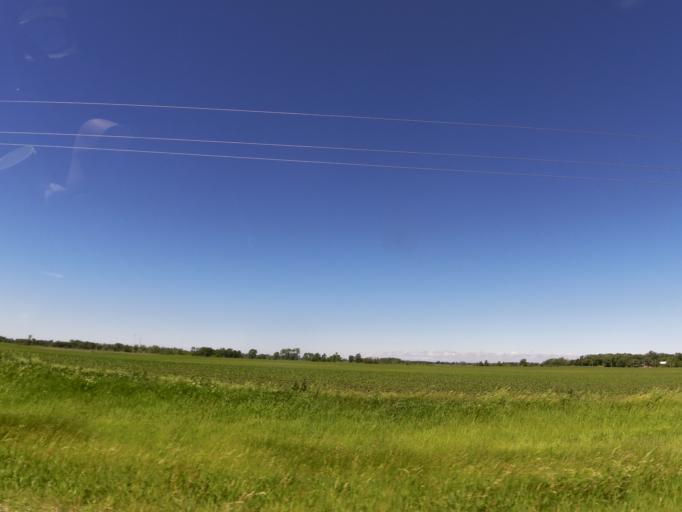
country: US
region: Minnesota
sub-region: Polk County
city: Fosston
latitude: 47.5684
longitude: -95.9820
